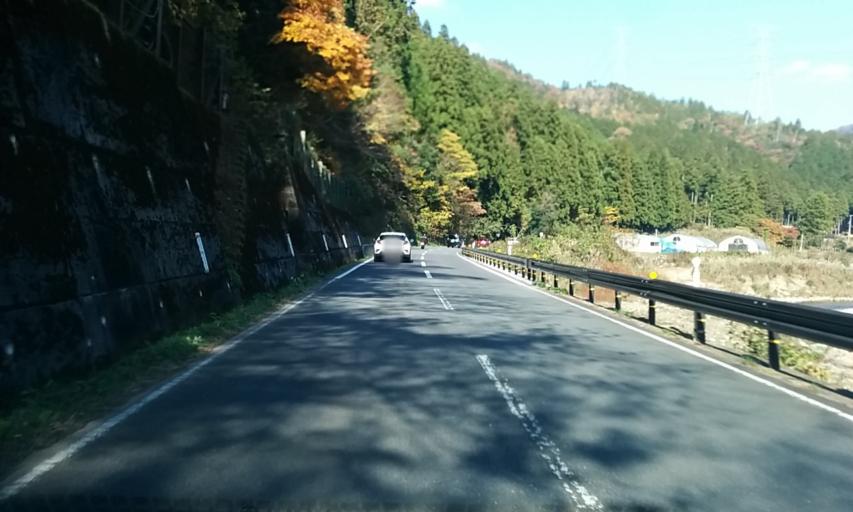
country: JP
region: Fukui
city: Obama
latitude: 35.3013
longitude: 135.6144
